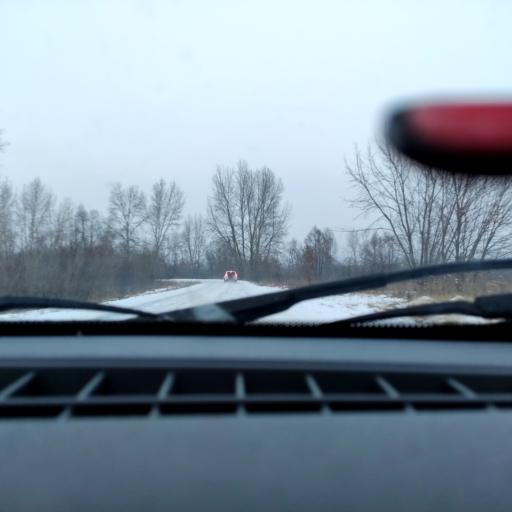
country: RU
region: Bashkortostan
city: Blagoveshchensk
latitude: 54.9037
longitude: 56.0126
